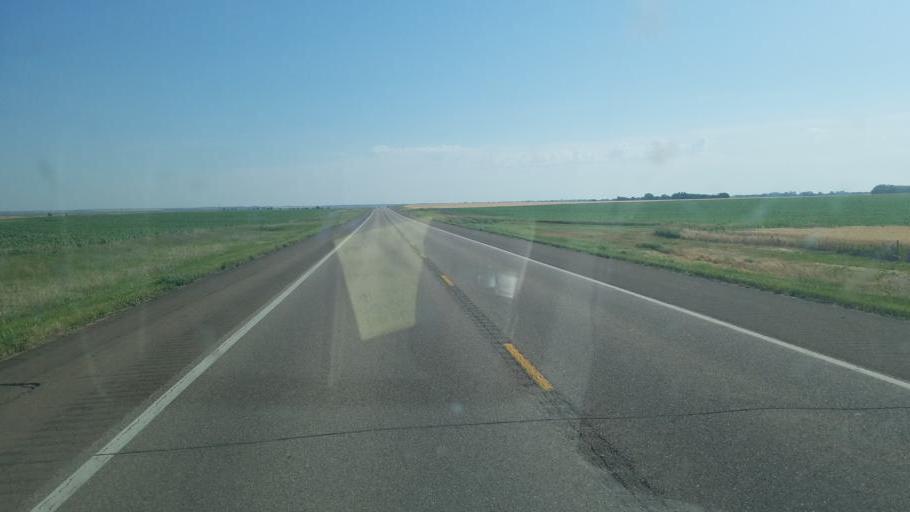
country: US
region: Kansas
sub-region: Barton County
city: Ellinwood
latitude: 38.4128
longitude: -98.6591
